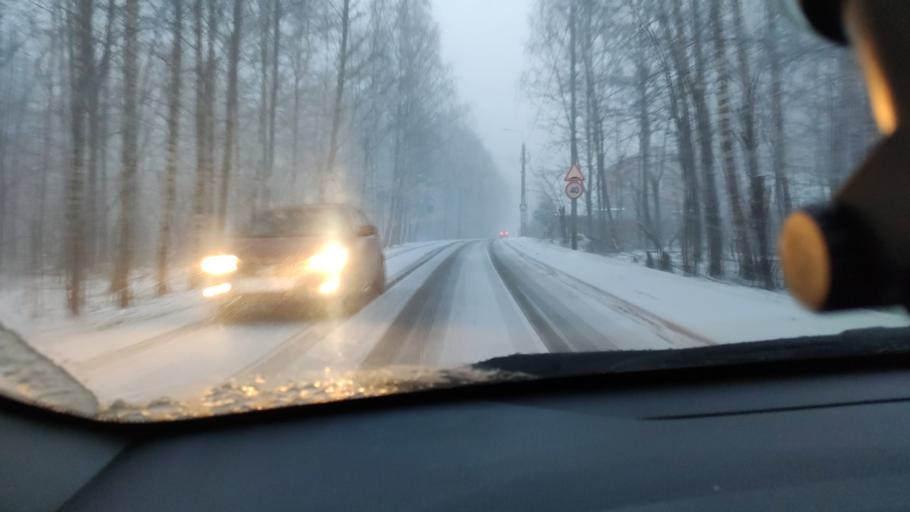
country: RU
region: Moscow
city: Annino
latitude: 55.5502
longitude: 37.6235
